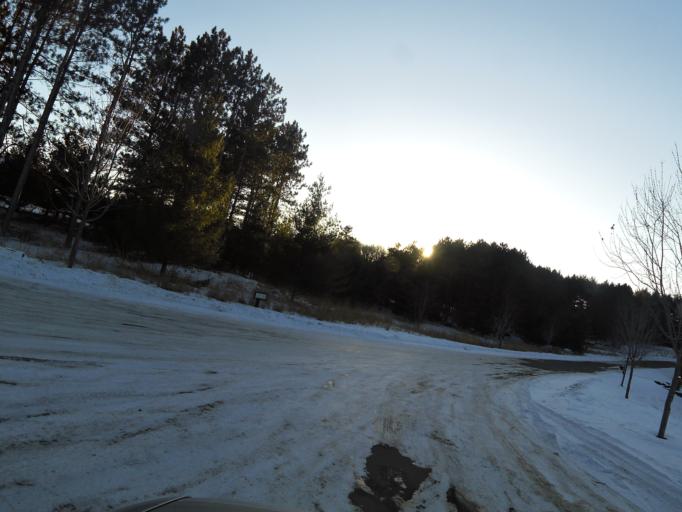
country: US
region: Minnesota
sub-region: Washington County
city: Lake Elmo
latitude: 44.9822
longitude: -92.8352
